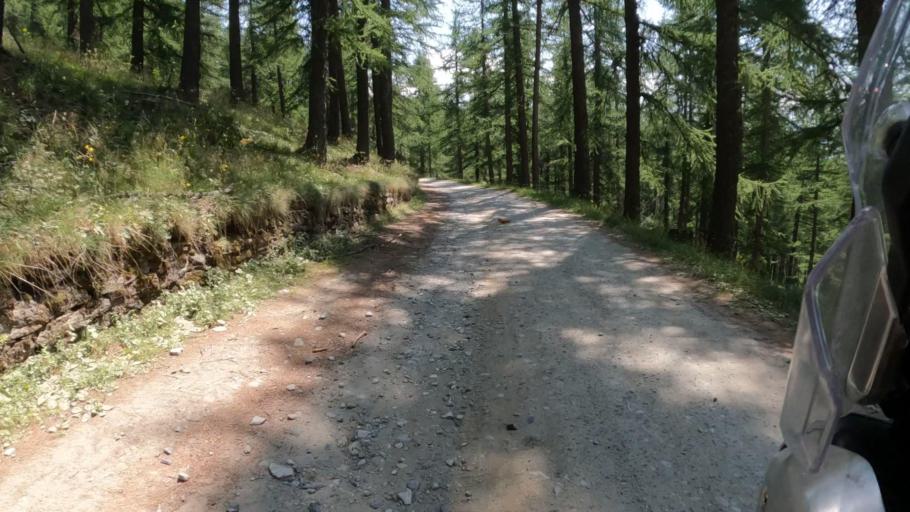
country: IT
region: Piedmont
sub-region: Provincia di Torino
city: Fenestrelle
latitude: 45.0468
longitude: 7.0796
